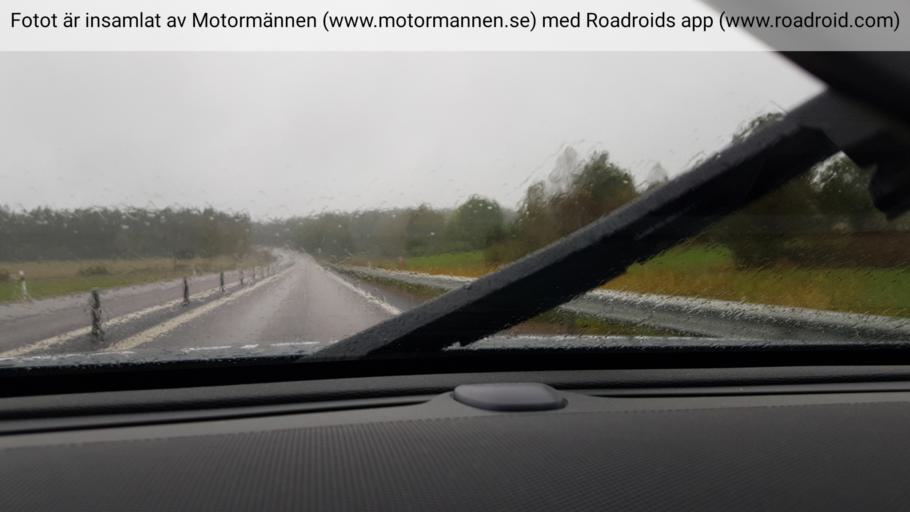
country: SE
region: Vaestra Goetaland
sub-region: Amals Kommun
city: Amal
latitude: 58.9501
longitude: 12.6049
